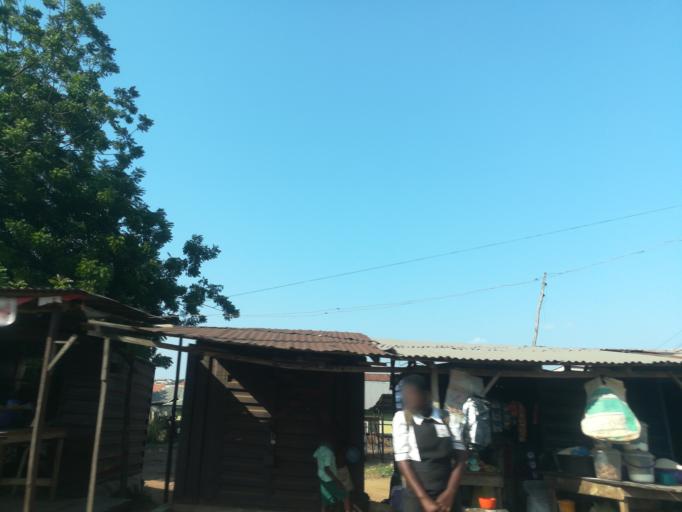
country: NG
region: Ogun
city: Abeokuta
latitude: 7.1359
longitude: 3.3032
